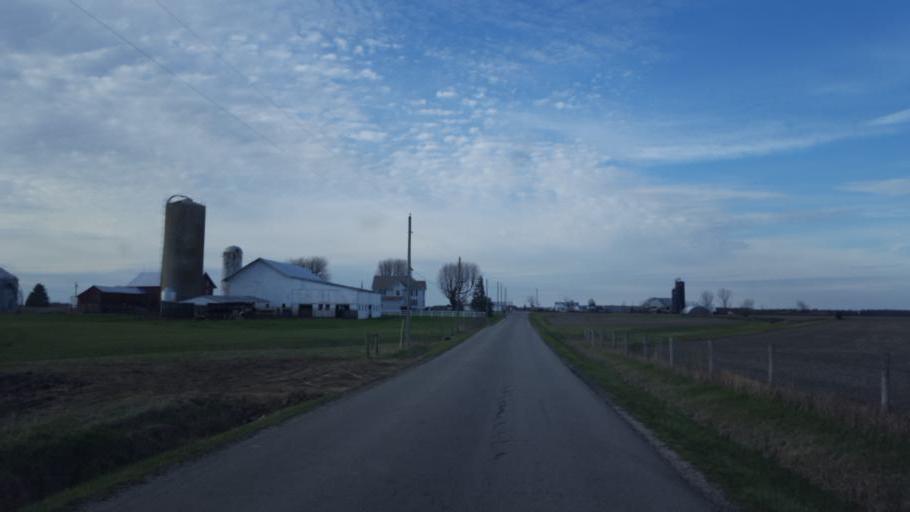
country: US
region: Ohio
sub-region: Crawford County
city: Bucyrus
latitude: 40.7963
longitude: -82.9018
